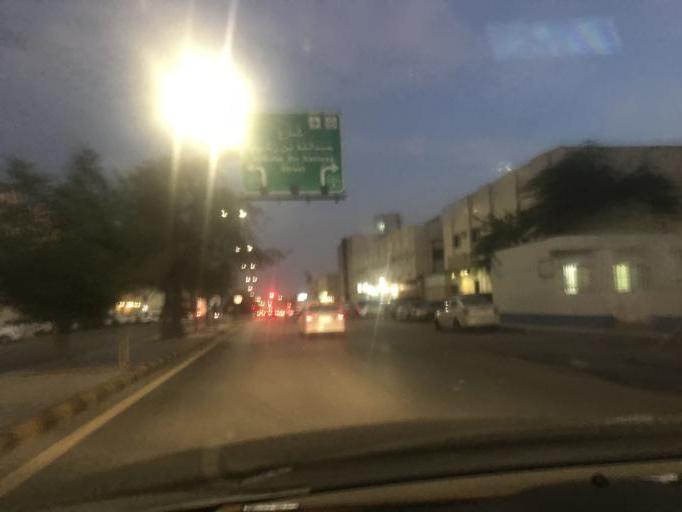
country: SA
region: Ar Riyad
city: Riyadh
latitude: 24.7327
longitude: 46.7608
